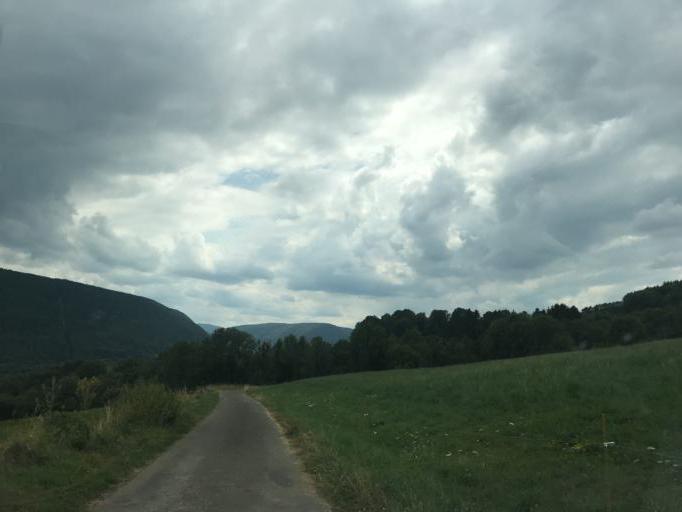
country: FR
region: Franche-Comte
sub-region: Departement du Jura
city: Longchaumois
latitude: 46.4680
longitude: 5.8924
